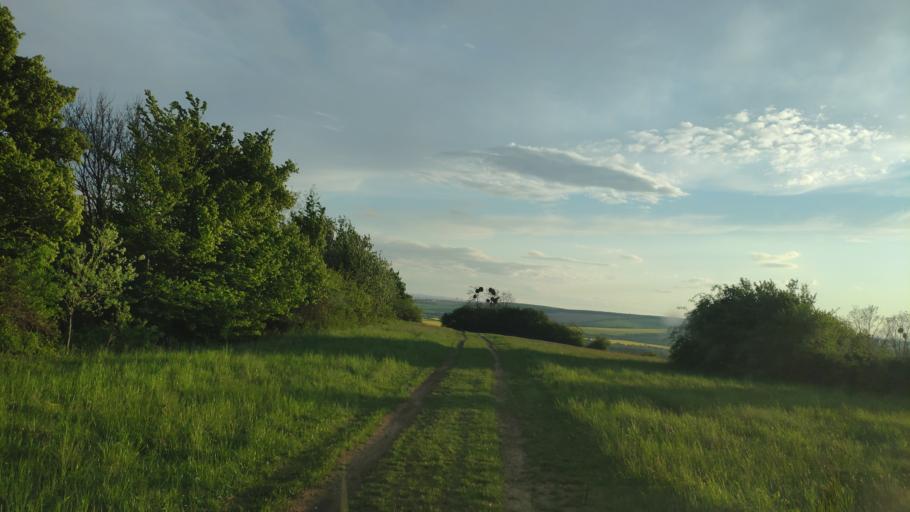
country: SK
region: Kosicky
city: Kosice
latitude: 48.7192
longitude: 21.3588
